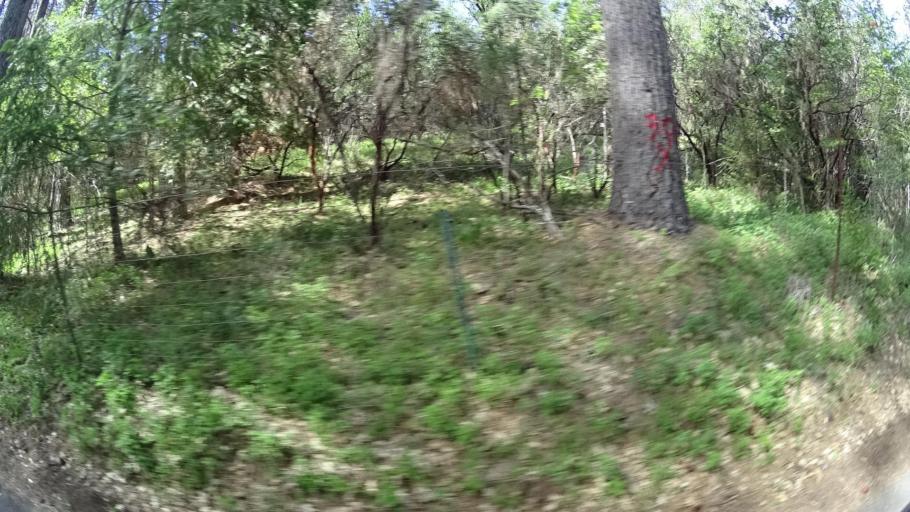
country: US
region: California
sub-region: Lake County
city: Cobb
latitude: 38.8807
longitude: -122.7700
